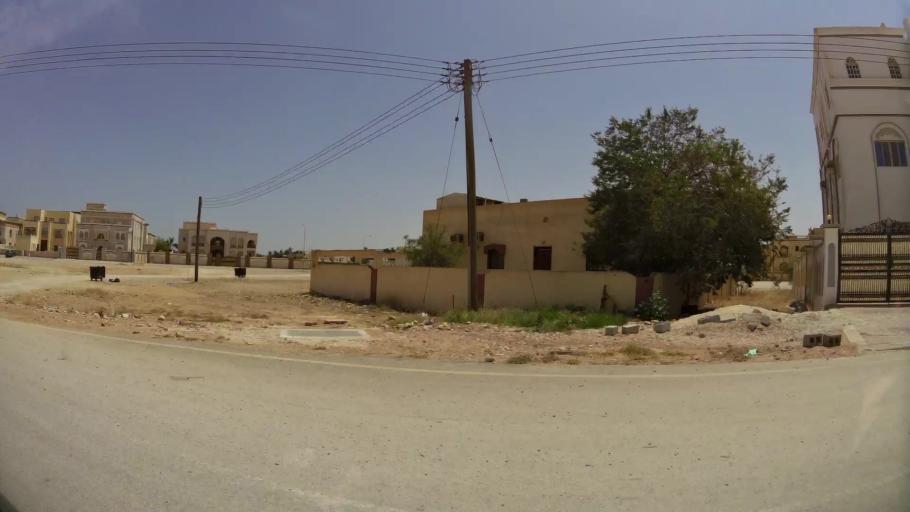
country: OM
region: Zufar
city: Salalah
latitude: 17.0634
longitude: 54.1580
